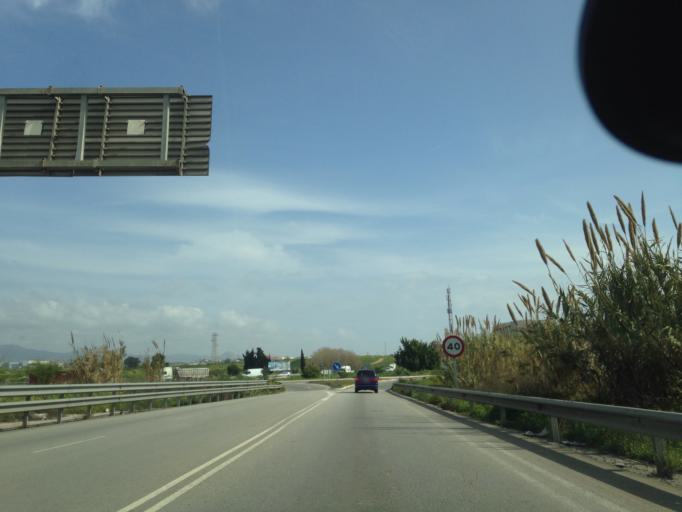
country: ES
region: Andalusia
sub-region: Provincia de Malaga
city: Alhaurin de la Torre
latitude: 36.7063
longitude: -4.5137
